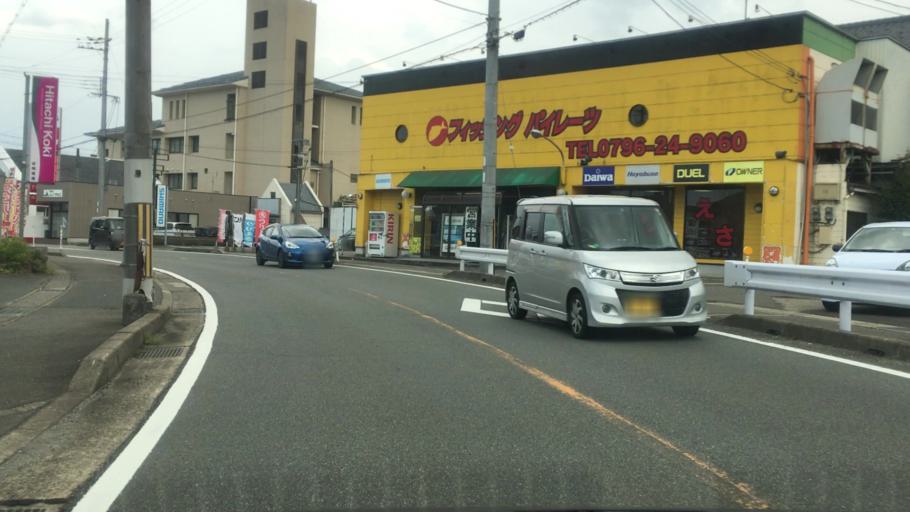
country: JP
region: Hyogo
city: Toyooka
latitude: 35.5349
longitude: 134.8184
